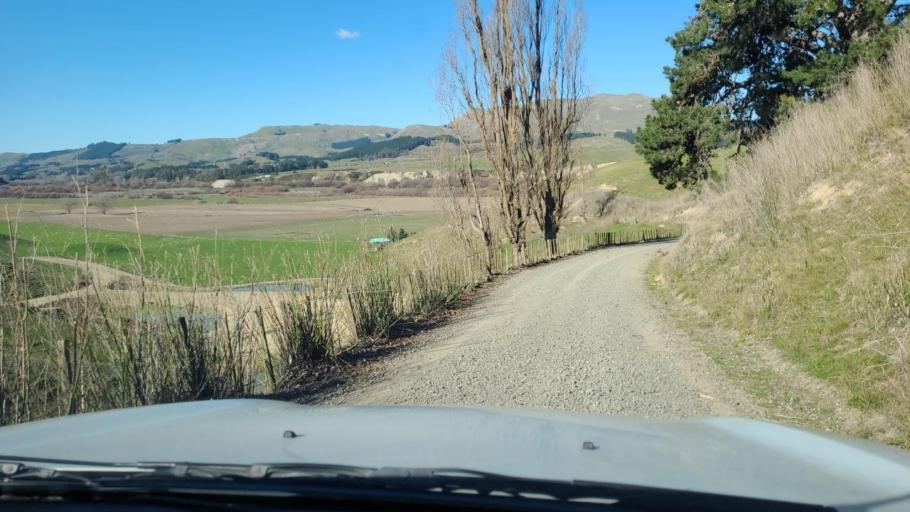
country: NZ
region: Hawke's Bay
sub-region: Hastings District
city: Hastings
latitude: -39.7617
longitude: 176.8065
